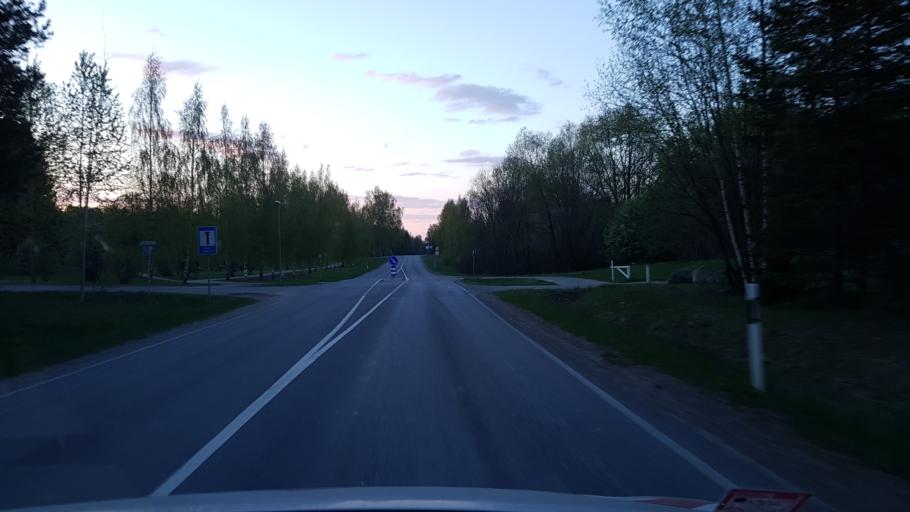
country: EE
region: Vorumaa
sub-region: Voru linn
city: Voru
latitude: 57.7938
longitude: 27.0342
